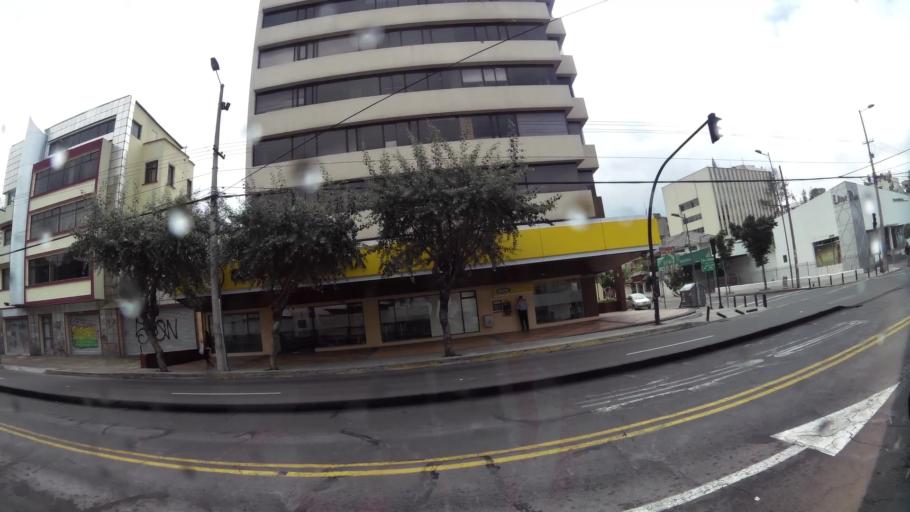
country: EC
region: Pichincha
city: Quito
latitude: -0.2073
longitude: -78.4940
